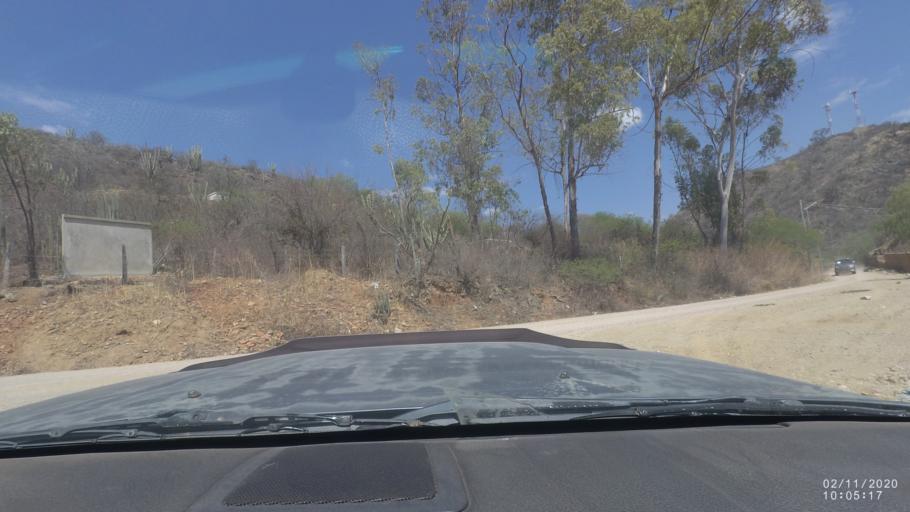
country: BO
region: Chuquisaca
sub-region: Provincia Zudanez
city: Mojocoya
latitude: -18.3221
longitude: -64.6778
